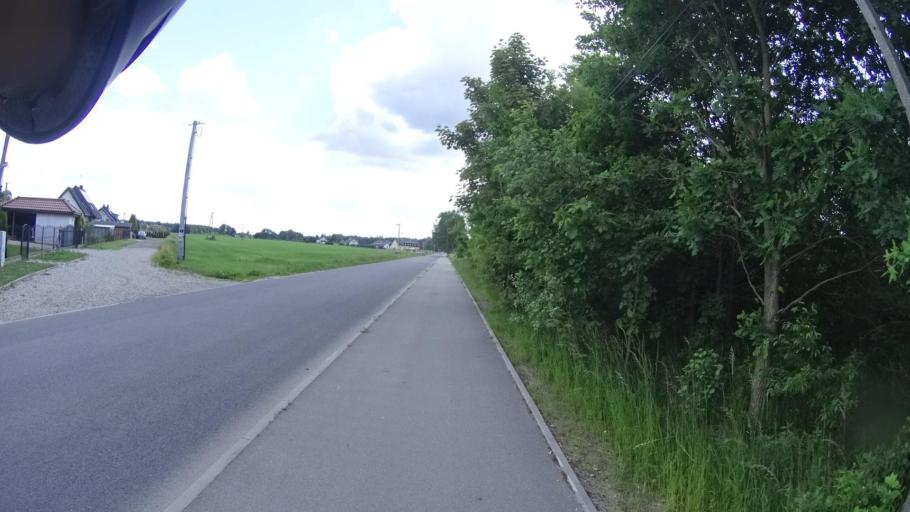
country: PL
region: Masovian Voivodeship
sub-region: Powiat pruszkowski
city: Nadarzyn
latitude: 52.0854
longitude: 20.8160
